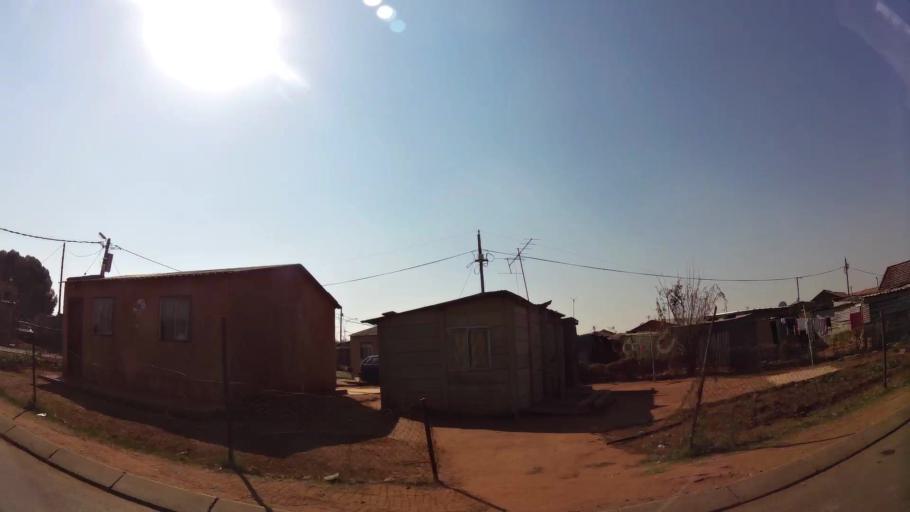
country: ZA
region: Gauteng
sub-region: Ekurhuleni Metropolitan Municipality
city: Boksburg
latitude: -26.2300
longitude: 28.2980
